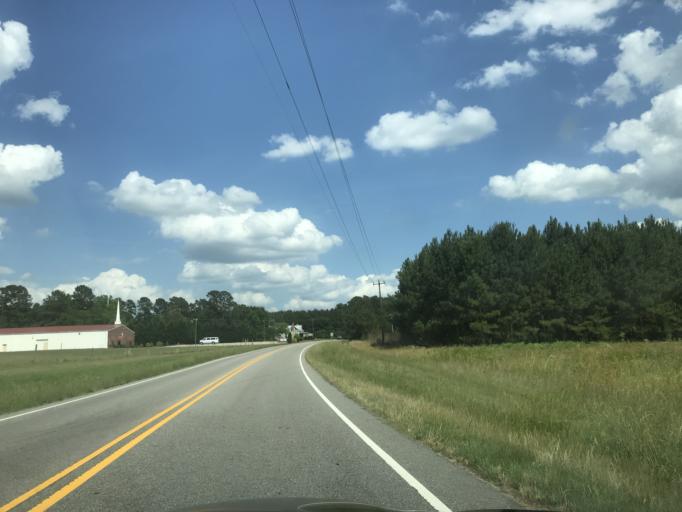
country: US
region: North Carolina
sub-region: Wake County
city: Rolesville
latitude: 35.9764
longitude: -78.3496
